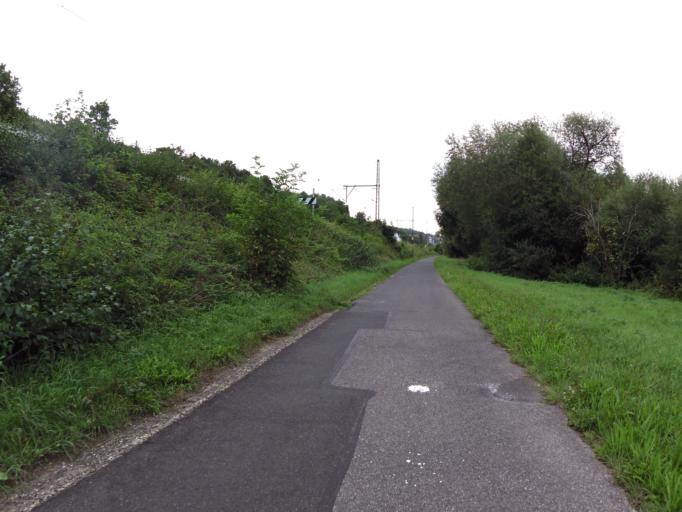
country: DE
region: Bavaria
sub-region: Regierungsbezirk Unterfranken
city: Schonungen
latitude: 50.0547
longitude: 10.2926
